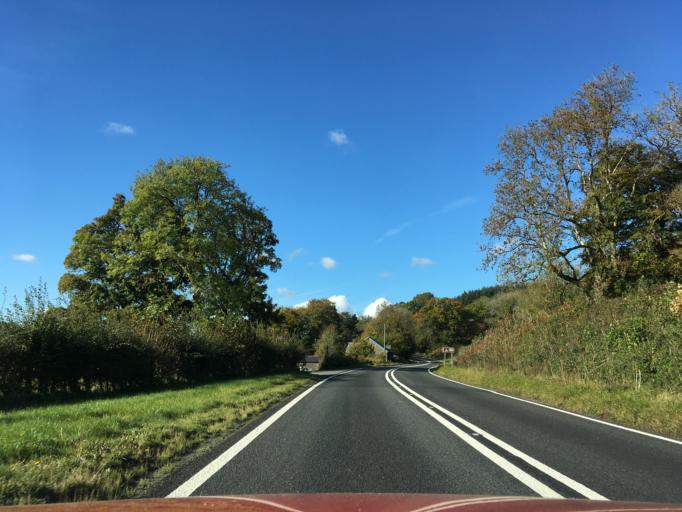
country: GB
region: Wales
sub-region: Merthyr Tydfil County Borough
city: Merthyr Tydfil
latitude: 51.7893
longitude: -3.4275
